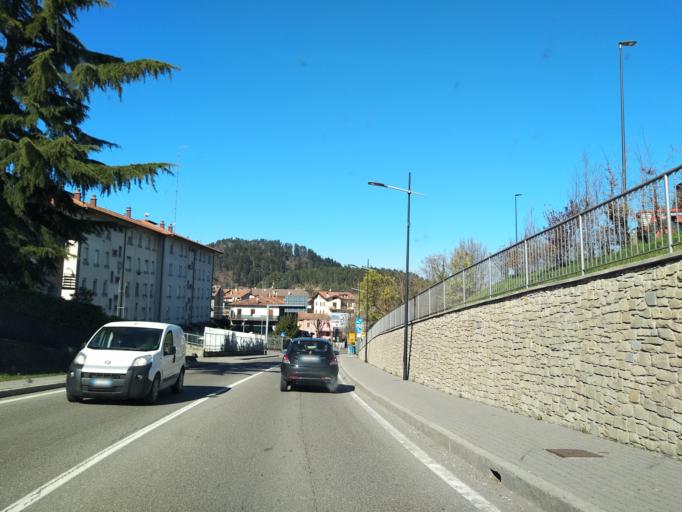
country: IT
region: Emilia-Romagna
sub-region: Provincia di Reggio Emilia
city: Castelnovo ne'Monti
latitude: 44.4325
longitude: 10.4101
